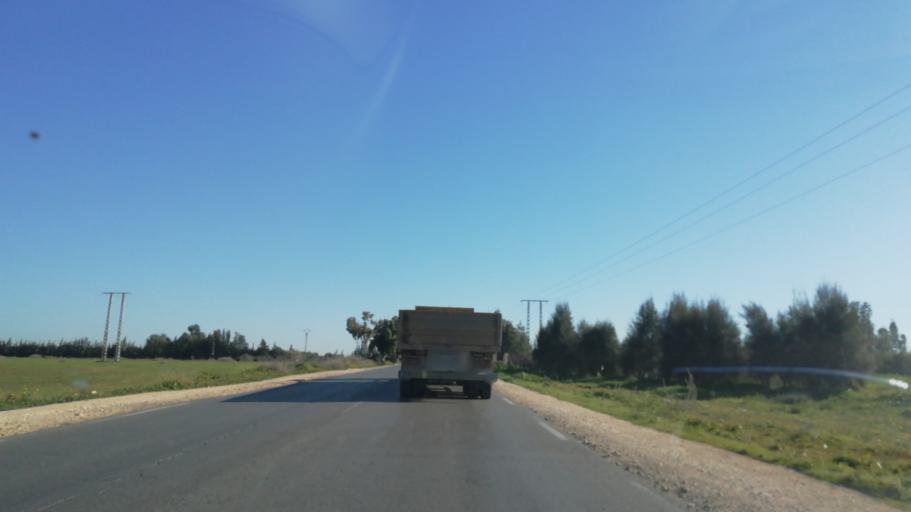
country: DZ
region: Relizane
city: Zemoura
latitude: 35.7487
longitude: 0.6920
